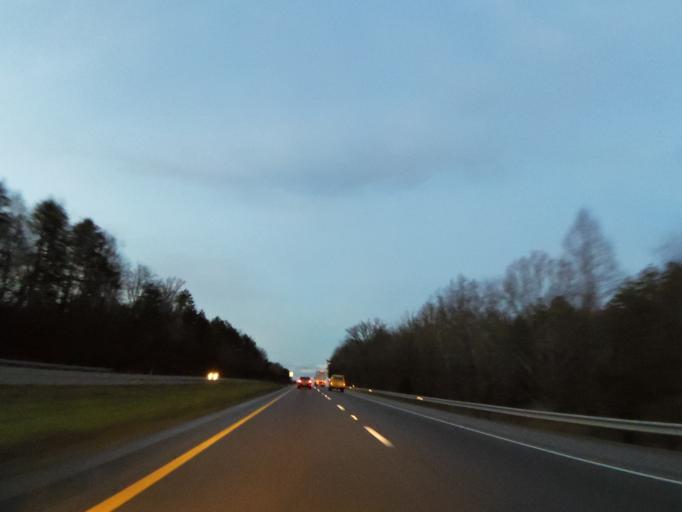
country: US
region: Kentucky
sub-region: Whitley County
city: Williamsburg
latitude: 36.8058
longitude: -84.1677
